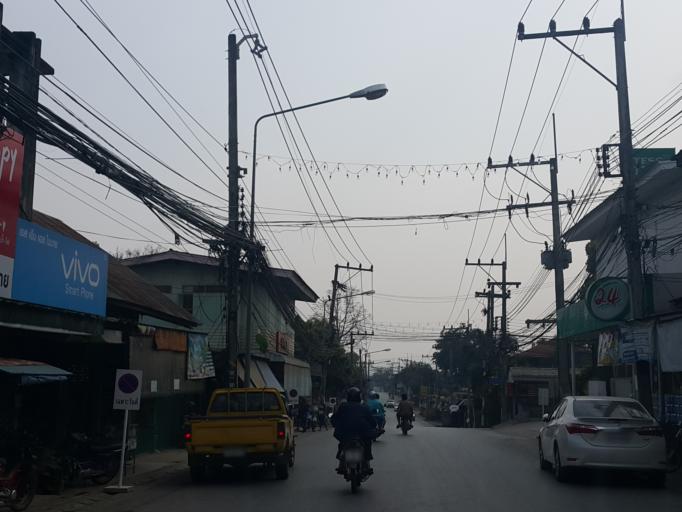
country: TH
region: Chiang Mai
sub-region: Amphoe Chiang Dao
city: Chiang Dao
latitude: 19.3680
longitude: 98.9649
